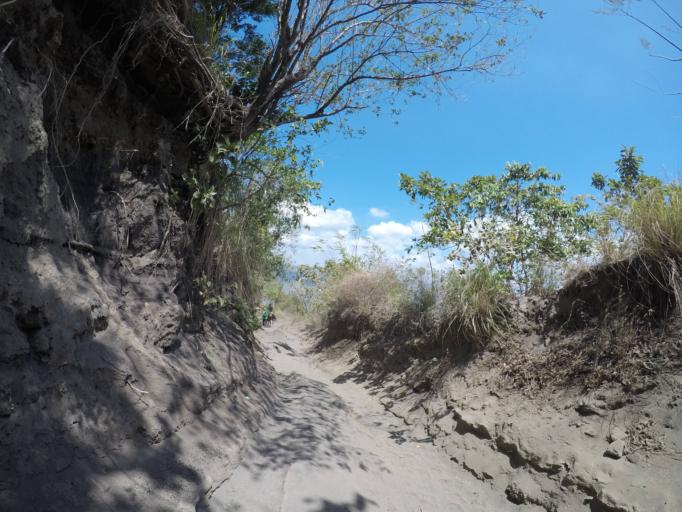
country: PH
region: Calabarzon
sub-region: Province of Batangas
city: Sampaloc
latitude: 14.0297
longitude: 121.0009
